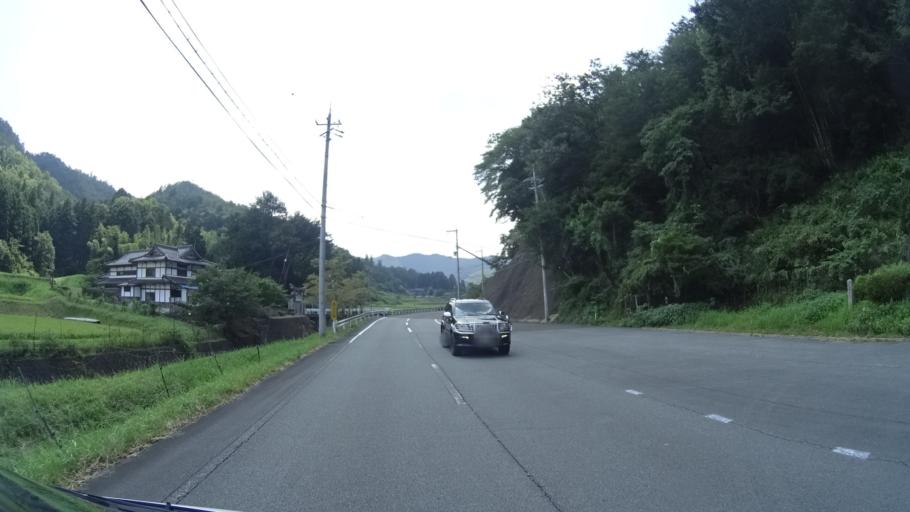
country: JP
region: Kyoto
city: Ayabe
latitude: 35.2104
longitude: 135.2016
